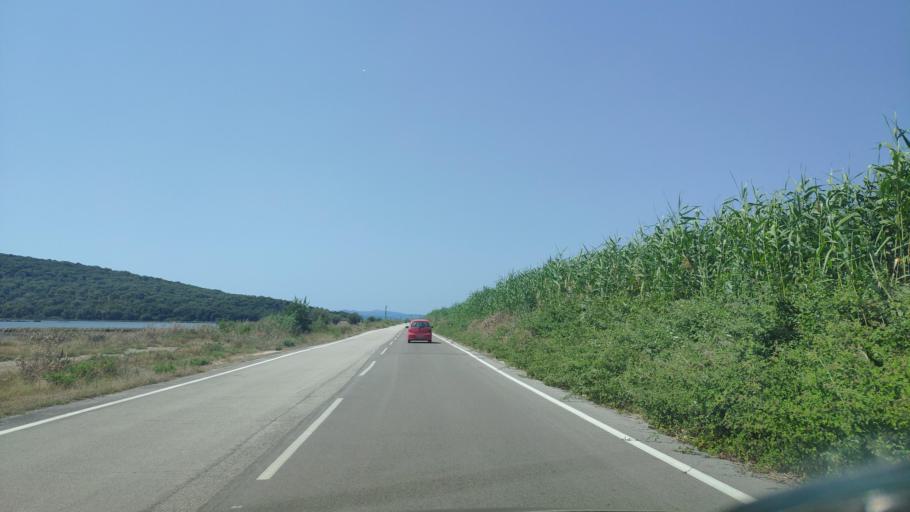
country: GR
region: Epirus
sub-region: Nomos Artas
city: Aneza
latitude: 39.0476
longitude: 20.8616
